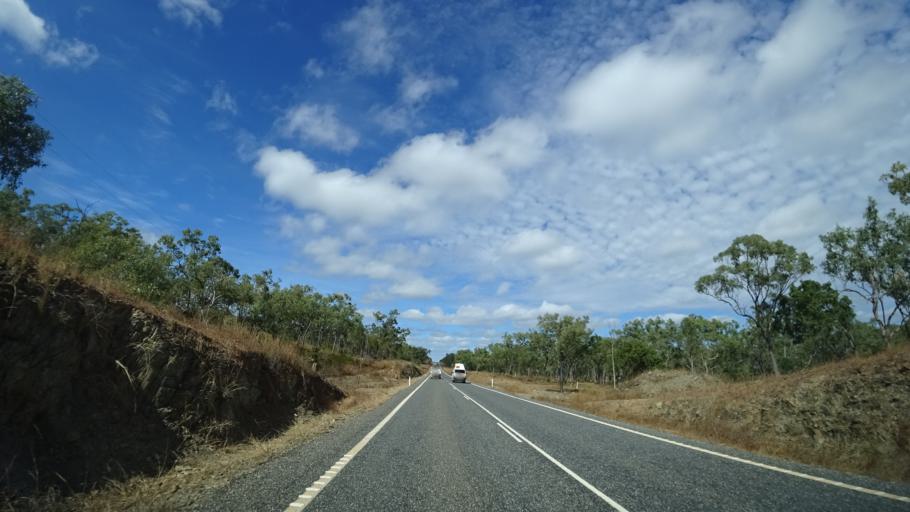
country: AU
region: Queensland
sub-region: Cairns
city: Port Douglas
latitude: -16.3106
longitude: 144.7176
